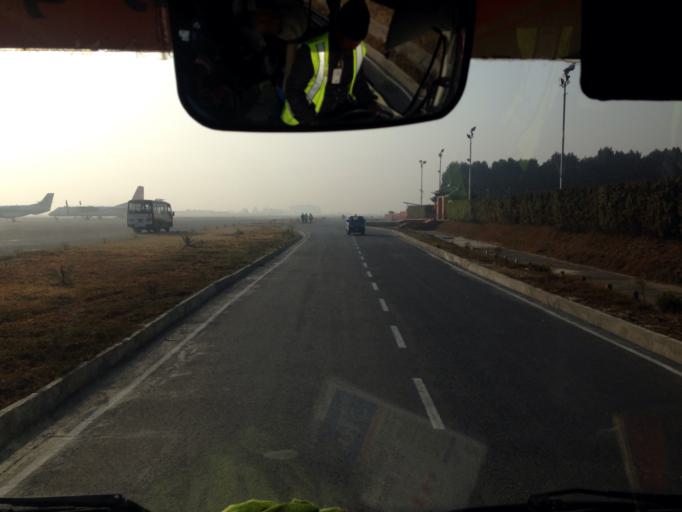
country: NP
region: Central Region
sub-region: Bagmati Zone
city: Kathmandu
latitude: 27.7060
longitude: 85.3592
